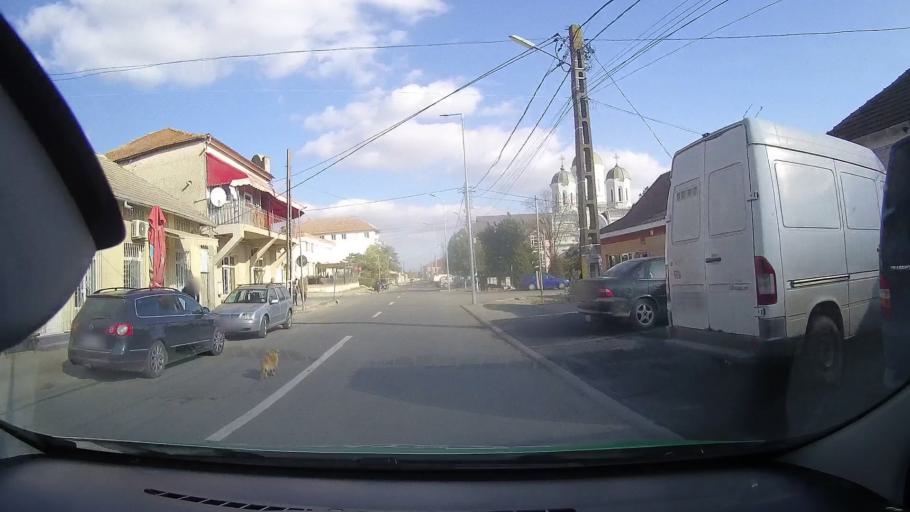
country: RO
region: Constanta
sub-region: Comuna Cogealac
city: Cogealac
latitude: 44.5564
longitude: 28.5634
